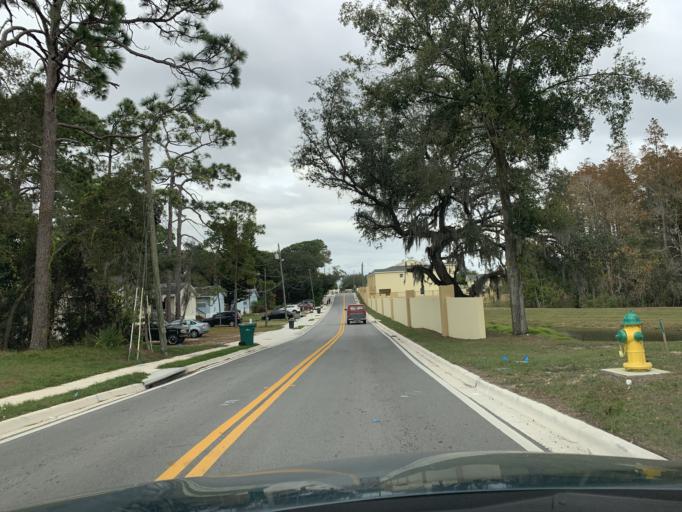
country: US
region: Florida
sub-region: Pinellas County
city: Tarpon Springs
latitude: 28.1527
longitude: -82.7383
